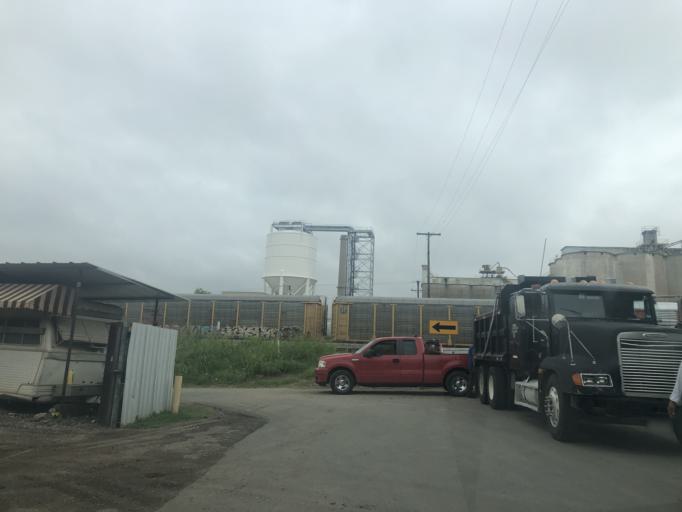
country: US
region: Texas
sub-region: Dallas County
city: Cockrell Hill
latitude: 32.7761
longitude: -96.8609
